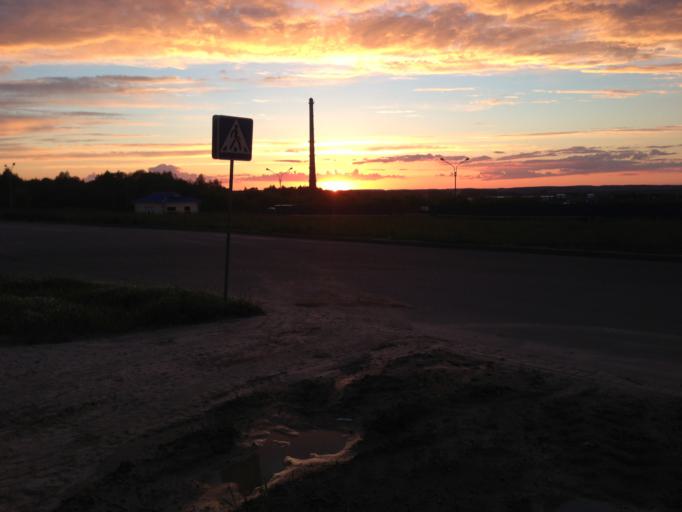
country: BY
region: Grodnenskaya
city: Hrodna
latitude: 53.7160
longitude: 23.8367
